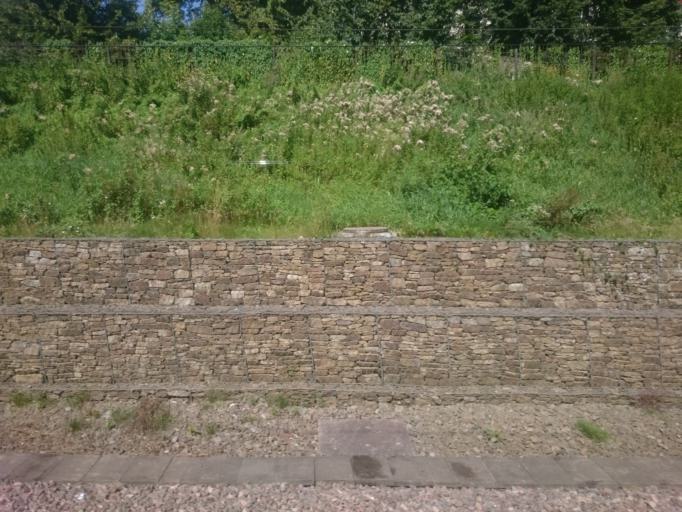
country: RU
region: Kaliningrad
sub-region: Gorod Kaliningrad
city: Kaliningrad
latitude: 54.7151
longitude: 20.4919
